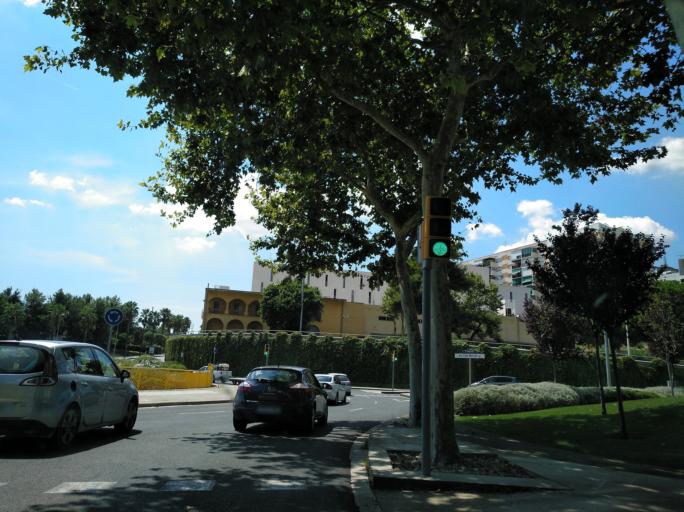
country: ES
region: Catalonia
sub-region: Provincia de Barcelona
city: Horta-Guinardo
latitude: 41.4339
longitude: 2.1525
